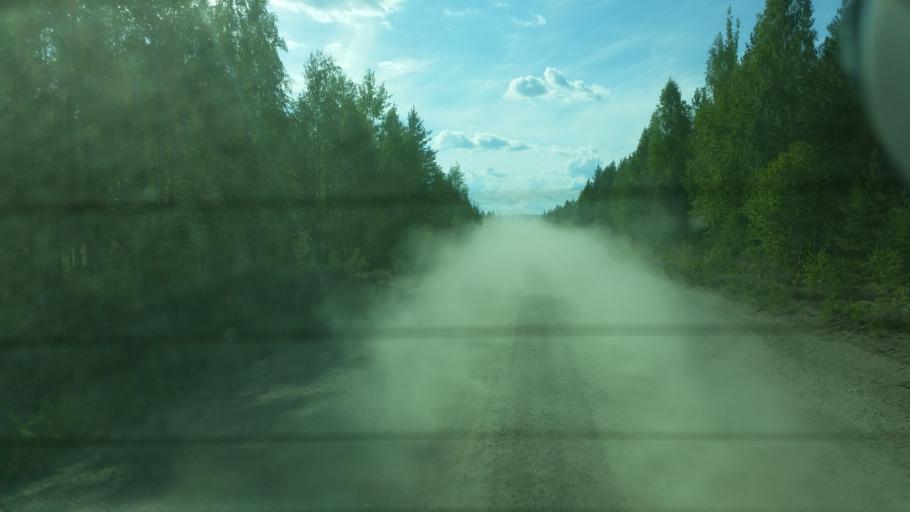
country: SE
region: Vaesternorrland
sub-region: Ange Kommun
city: Ange
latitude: 62.1995
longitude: 15.5731
